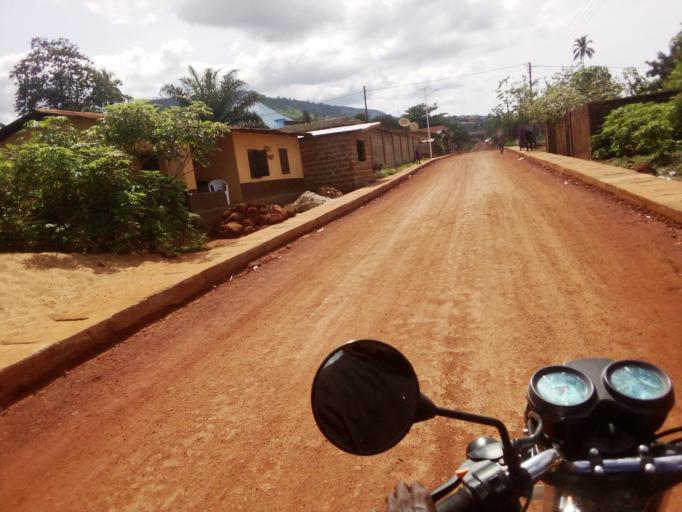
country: SL
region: Western Area
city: Waterloo
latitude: 8.3361
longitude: -13.0707
